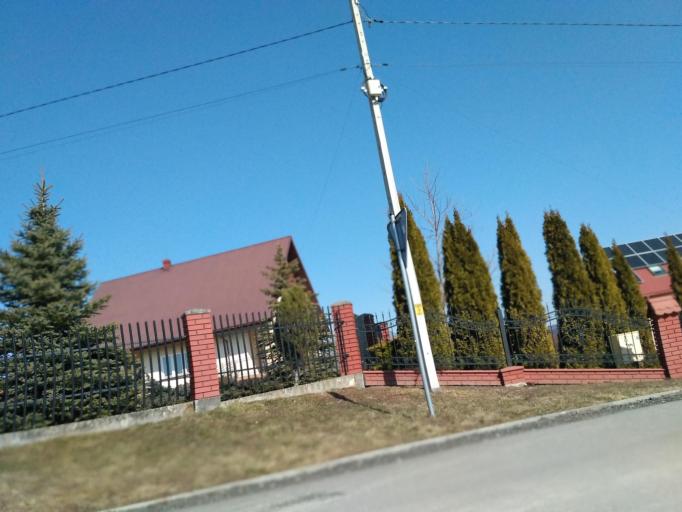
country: PL
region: Subcarpathian Voivodeship
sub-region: Powiat brzozowski
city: Jasienica Rosielna
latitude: 49.7558
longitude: 21.9392
